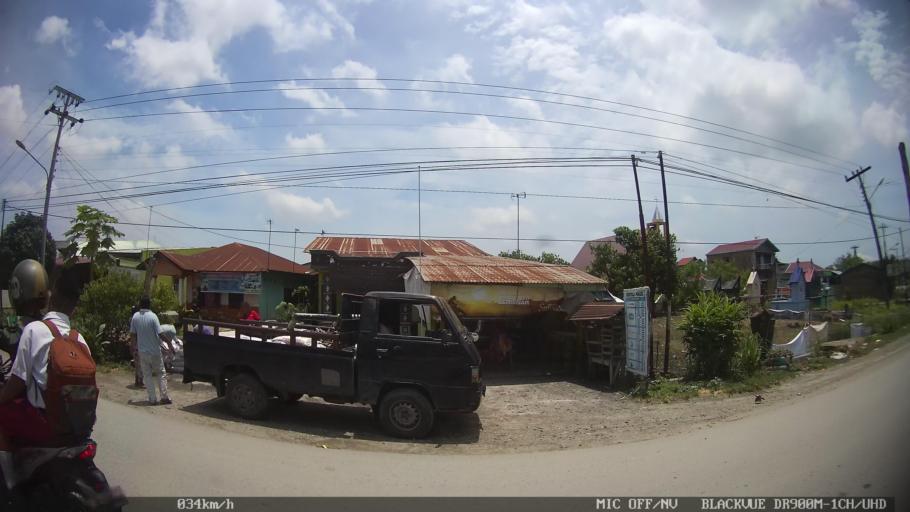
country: ID
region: North Sumatra
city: Perbaungan
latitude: 3.5376
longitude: 98.8824
